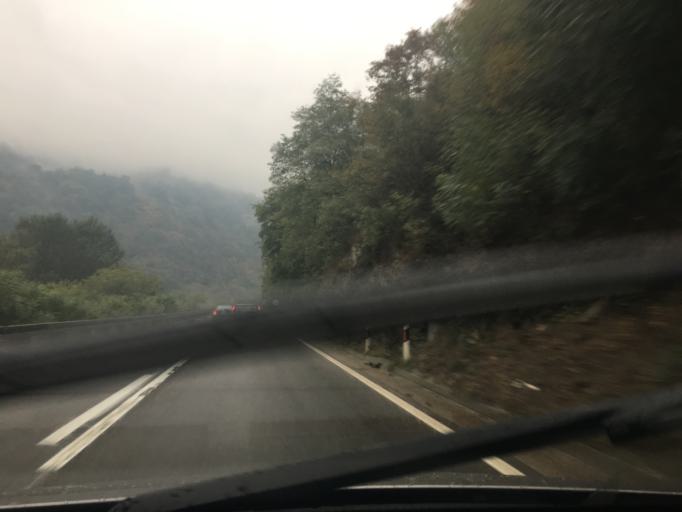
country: RS
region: Central Serbia
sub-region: Pcinjski Okrug
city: Vladicin Han
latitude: 42.7338
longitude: 22.0623
